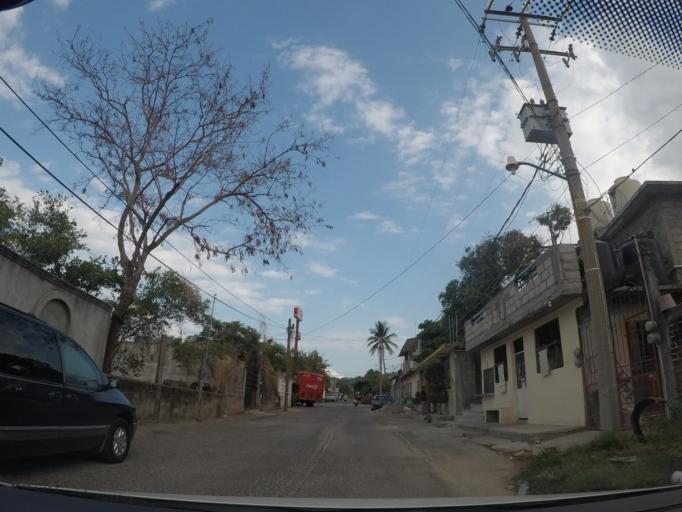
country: MX
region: Oaxaca
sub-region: Salina Cruz
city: Salina Cruz
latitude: 16.2062
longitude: -95.2089
